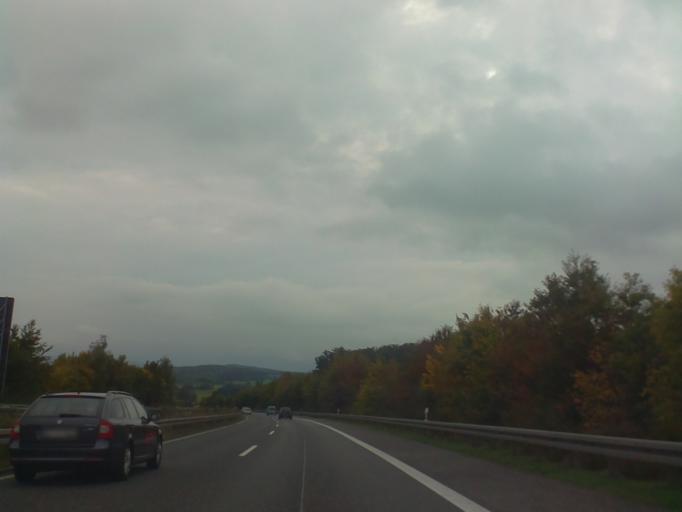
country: DE
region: Hesse
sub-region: Regierungsbezirk Darmstadt
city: Schluchtern
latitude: 50.3794
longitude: 9.5183
